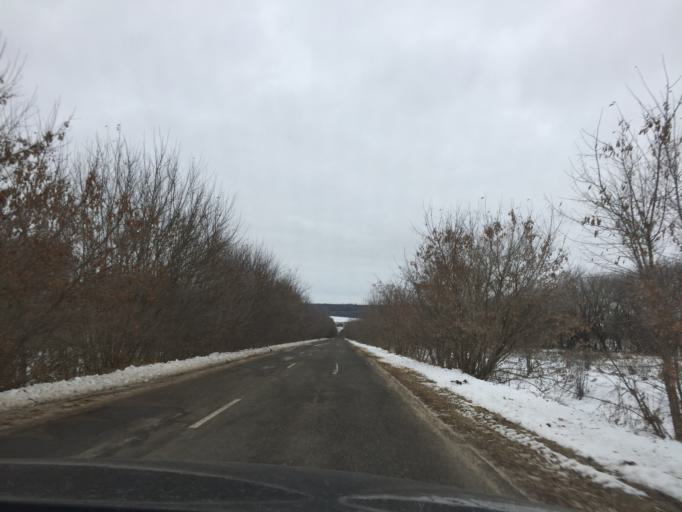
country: RU
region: Tula
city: Teploye
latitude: 53.7797
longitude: 37.6316
